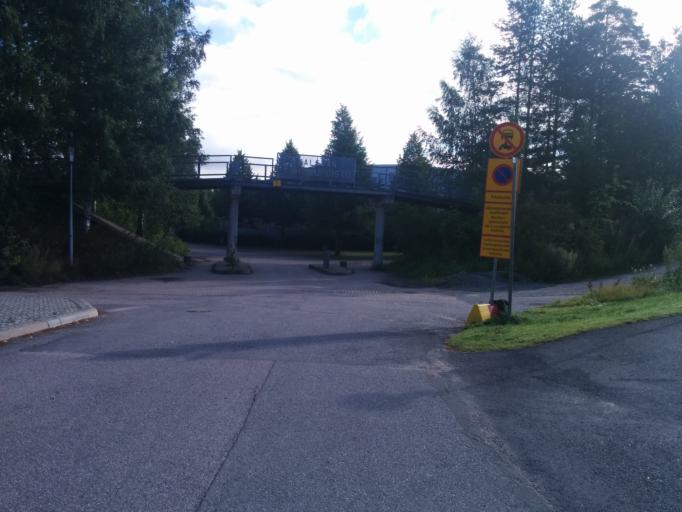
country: FI
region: Uusimaa
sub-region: Helsinki
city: Kerava
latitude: 60.4090
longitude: 25.0911
